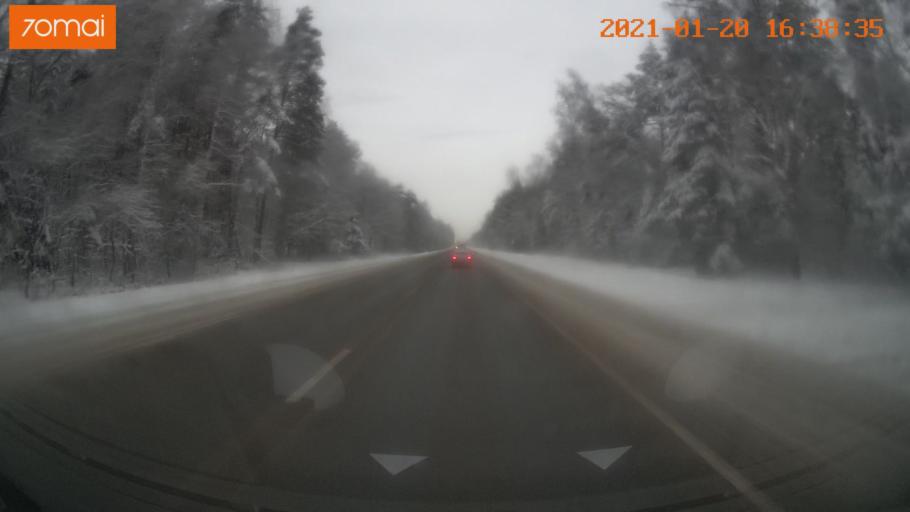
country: RU
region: Vladimir
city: Orgtrud
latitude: 56.2066
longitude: 40.6996
